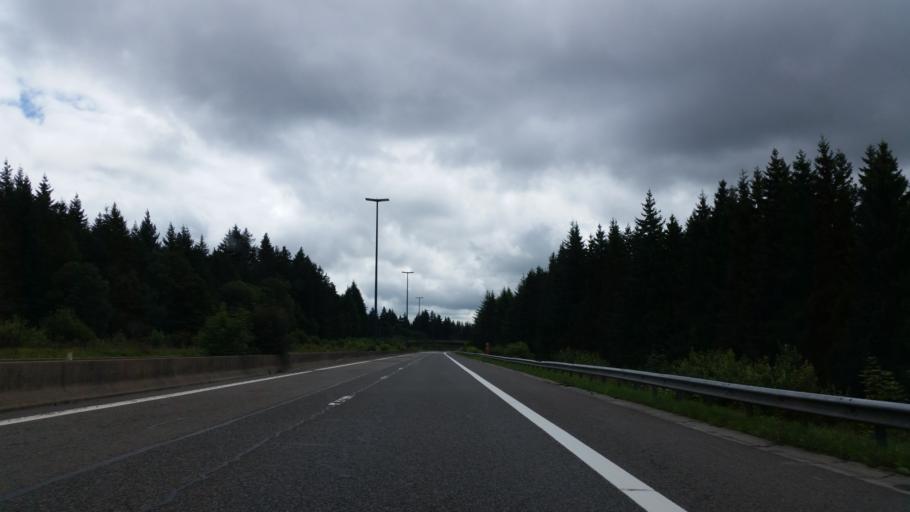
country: BE
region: Wallonia
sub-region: Province du Luxembourg
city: Houffalize
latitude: 50.2074
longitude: 5.7772
